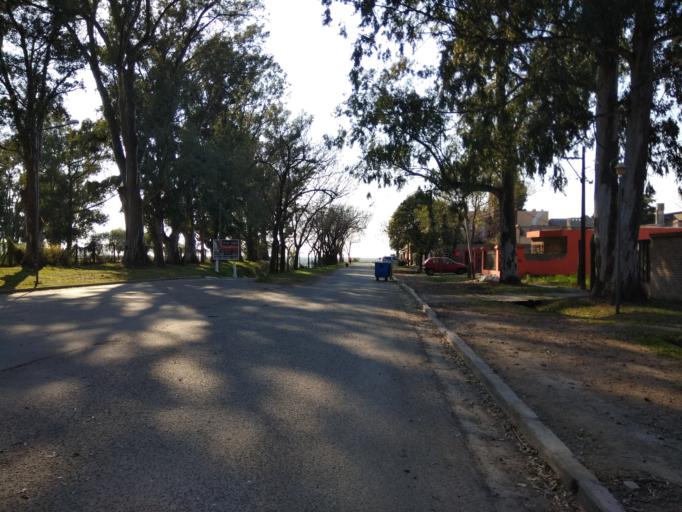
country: AR
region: Santa Fe
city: Granadero Baigorria
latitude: -32.8473
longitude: -60.6985
